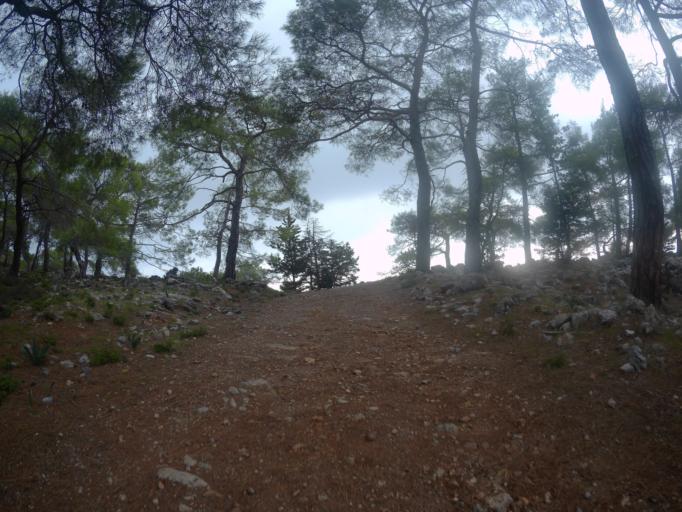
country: CY
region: Ammochostos
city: Lefkonoiko
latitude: 35.3035
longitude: 33.5793
